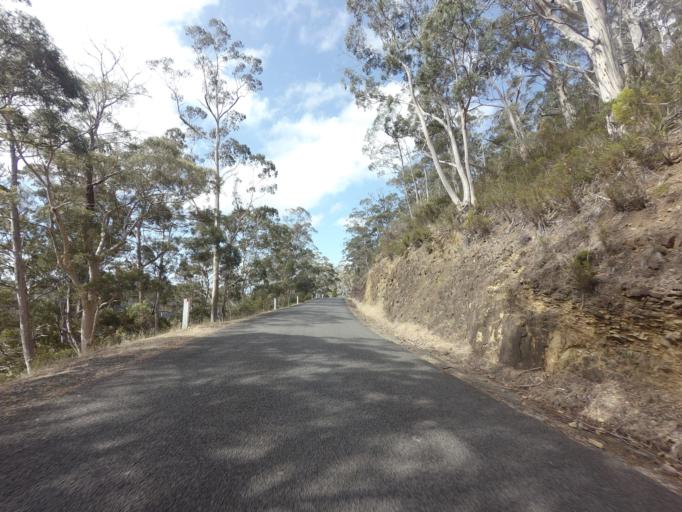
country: AU
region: Tasmania
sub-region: Hobart
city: Dynnyrne
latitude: -42.9178
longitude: 147.2722
